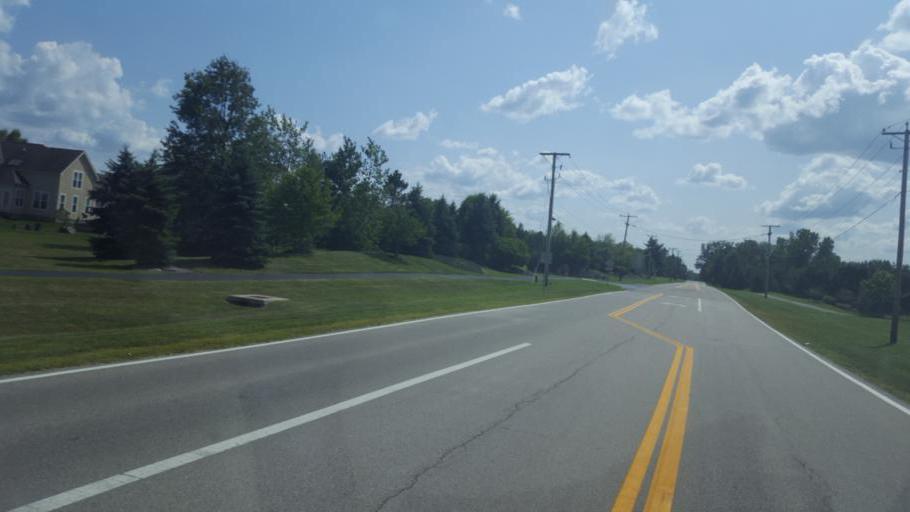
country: US
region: Ohio
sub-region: Delaware County
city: Lewis Center
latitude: 40.2544
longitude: -82.9554
